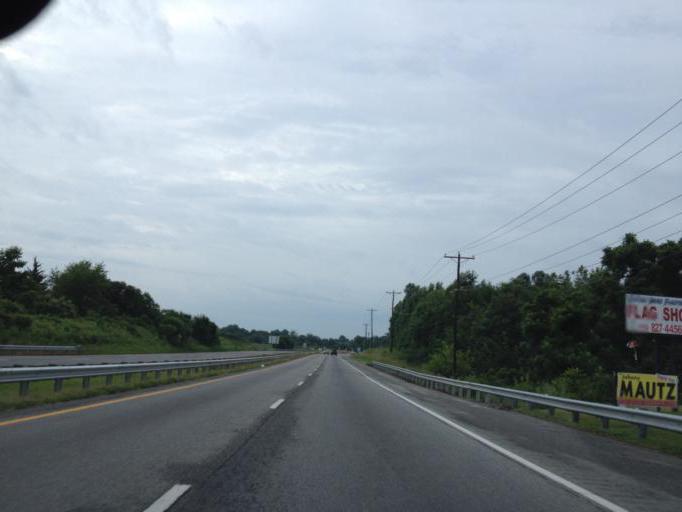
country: US
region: Maryland
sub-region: Queen Anne's County
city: Centreville
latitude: 38.9537
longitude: -76.0762
